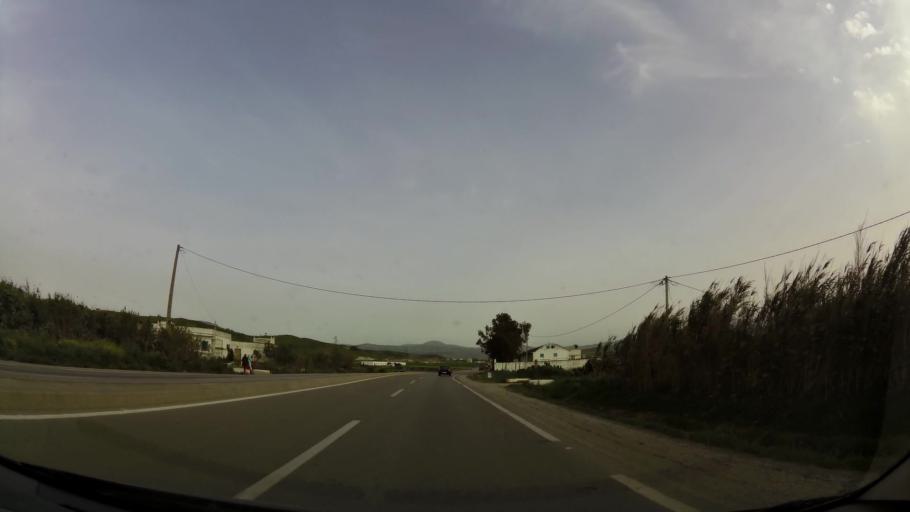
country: MA
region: Tanger-Tetouan
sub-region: Tanger-Assilah
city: Dar Chaoui
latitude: 35.6003
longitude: -5.6522
